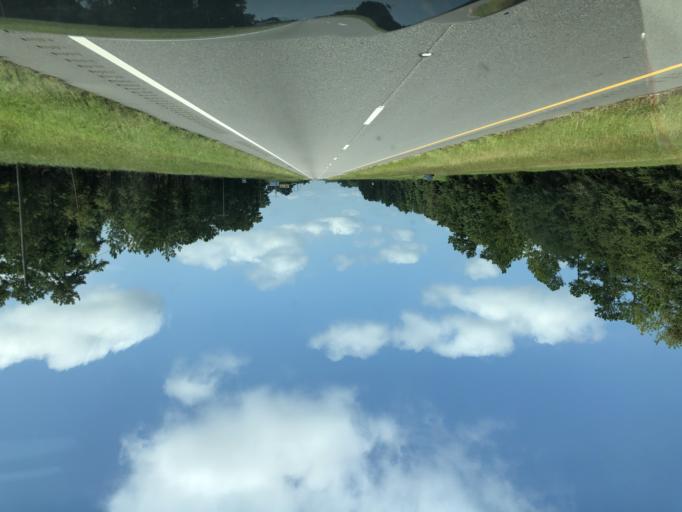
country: US
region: Alabama
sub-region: Houston County
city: Rehobeth
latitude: 31.0407
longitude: -85.4061
